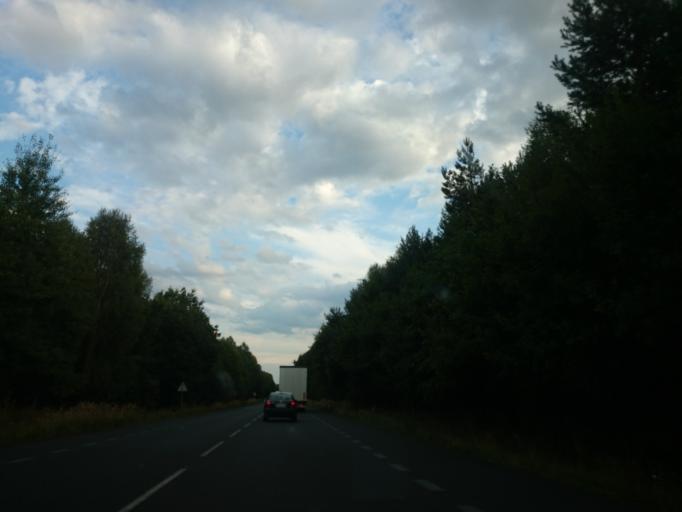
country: PL
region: Lubusz
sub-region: Powiat gorzowski
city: Jenin
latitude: 52.8048
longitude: 15.0982
